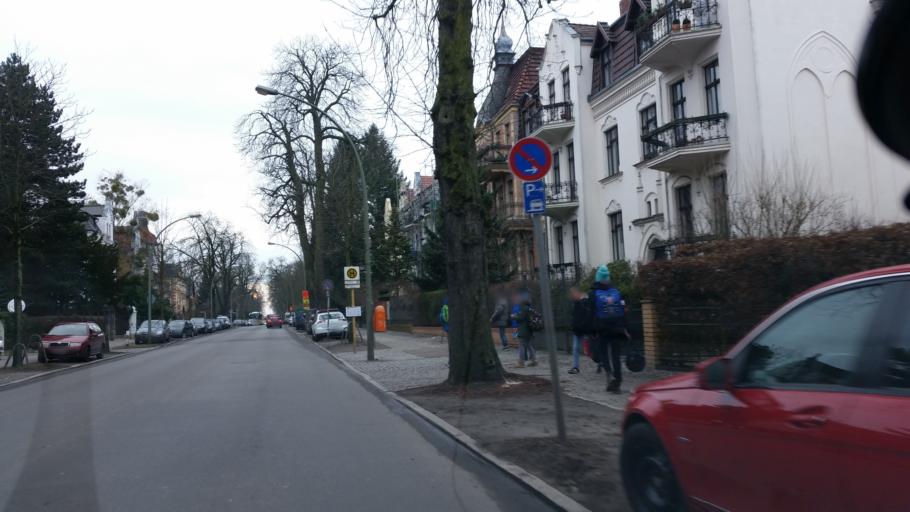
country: DE
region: Berlin
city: Lichterfelde
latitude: 52.4377
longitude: 13.3025
